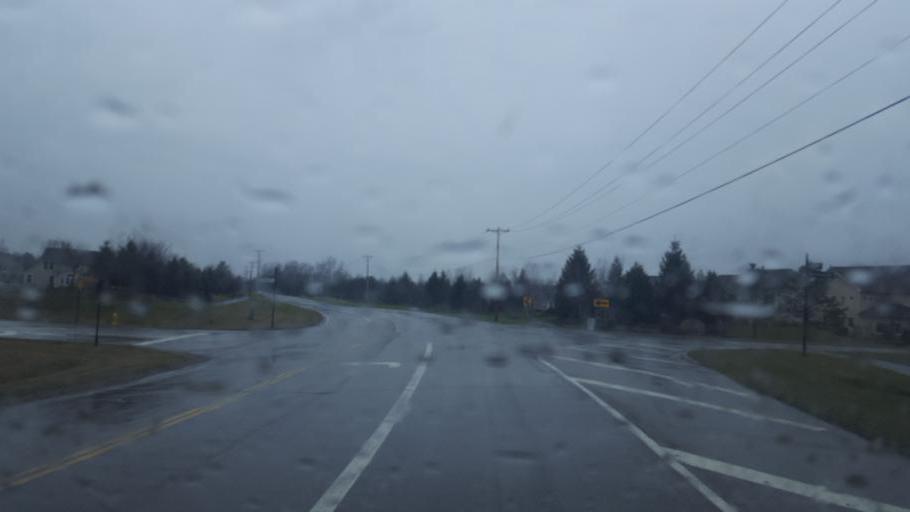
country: US
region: Ohio
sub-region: Delaware County
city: Lewis Center
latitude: 40.2552
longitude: -82.9547
